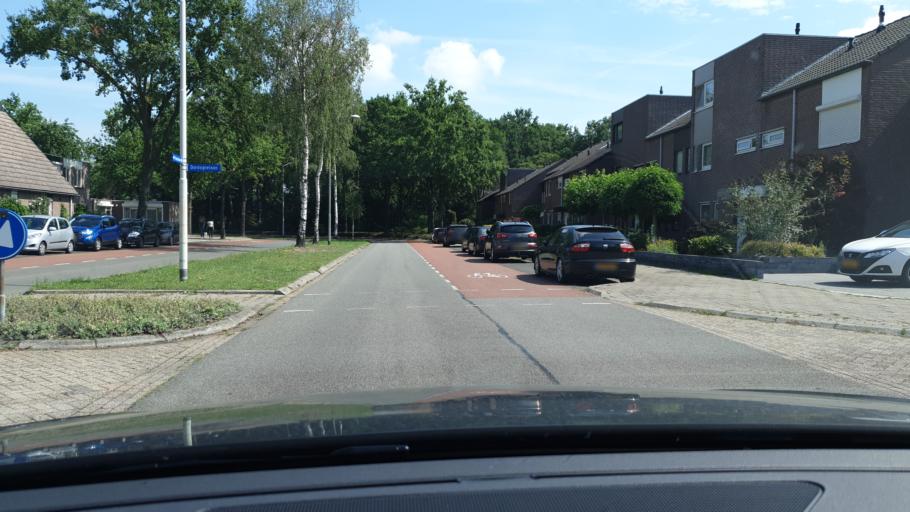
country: NL
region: North Brabant
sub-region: Gemeente Eindhoven
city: Eindhoven
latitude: 51.4796
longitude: 5.4492
